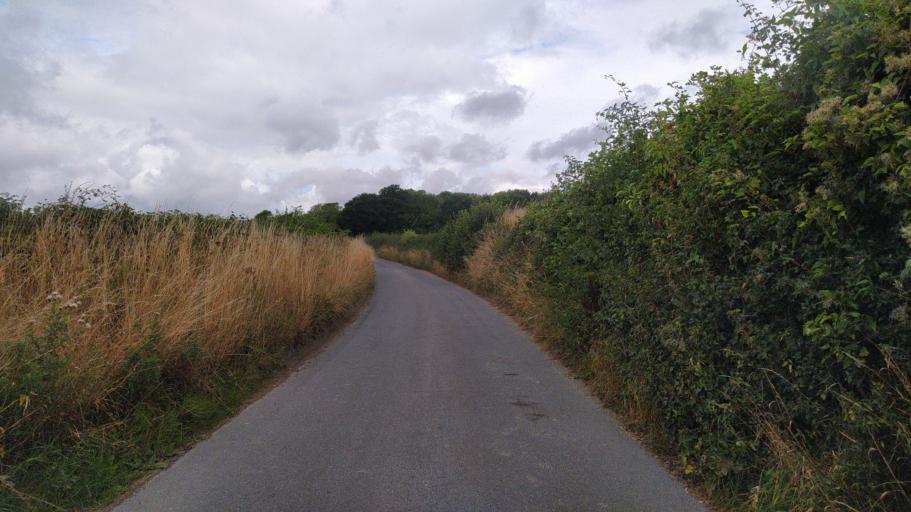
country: GB
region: England
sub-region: Hampshire
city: Petersfield
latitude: 50.9868
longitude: -0.9688
